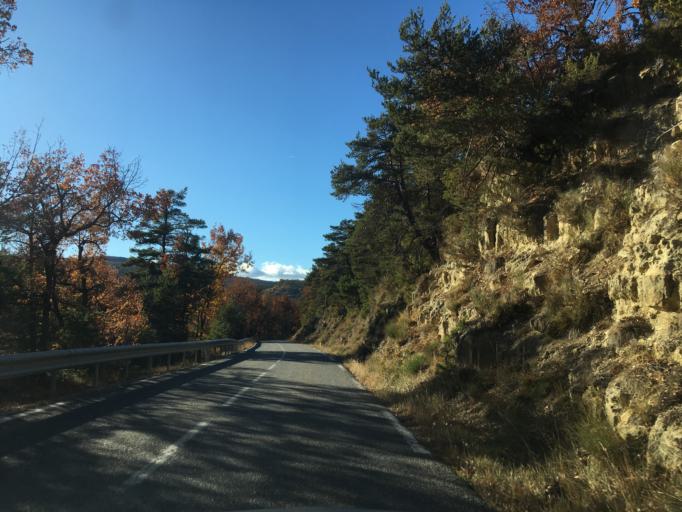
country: FR
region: Provence-Alpes-Cote d'Azur
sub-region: Departement des Alpes-de-Haute-Provence
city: Castellane
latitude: 43.7409
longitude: 6.4900
